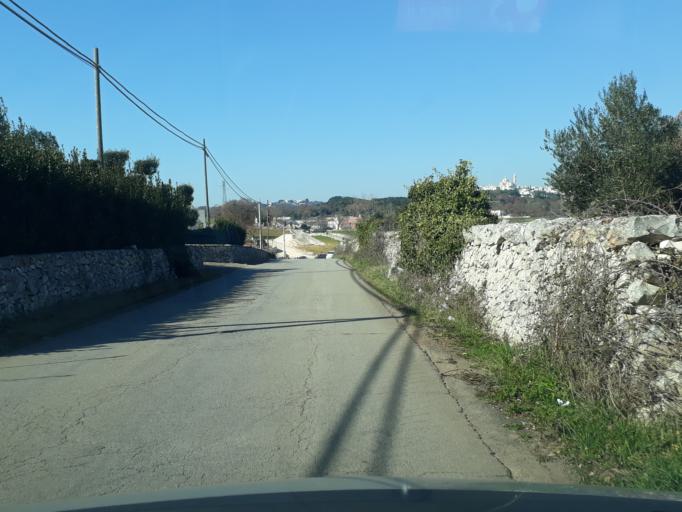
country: IT
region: Apulia
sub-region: Provincia di Bari
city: Locorotondo
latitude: 40.7434
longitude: 17.3480
